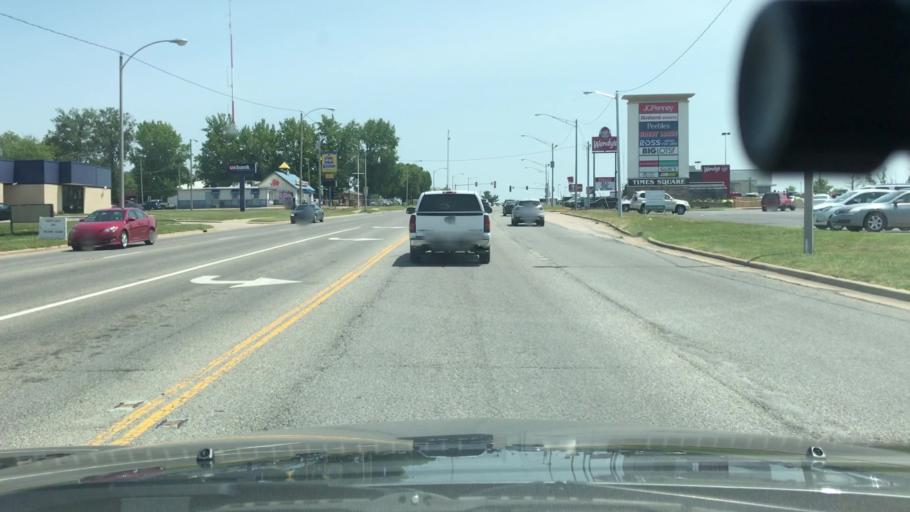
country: US
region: Illinois
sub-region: Jefferson County
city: Mount Vernon
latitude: 38.3142
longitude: -88.9419
